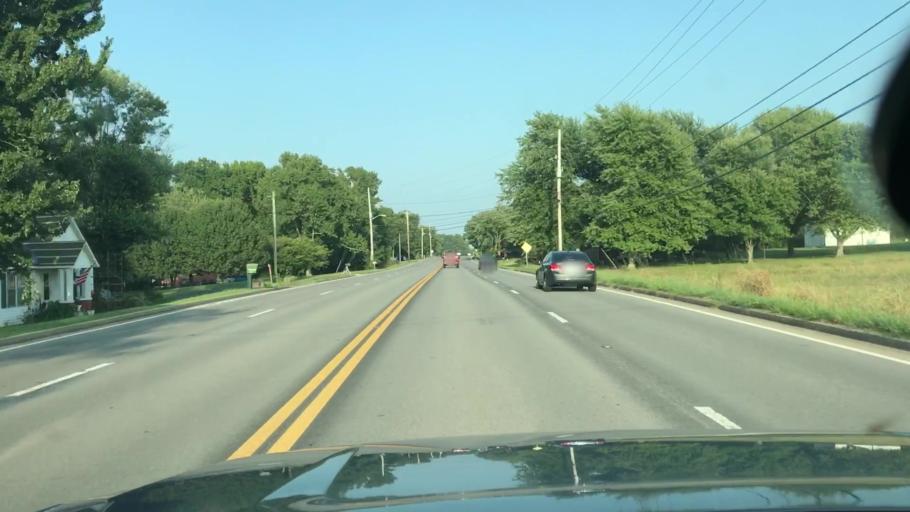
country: US
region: Tennessee
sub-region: Sumner County
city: Portland
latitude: 36.5780
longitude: -86.4934
